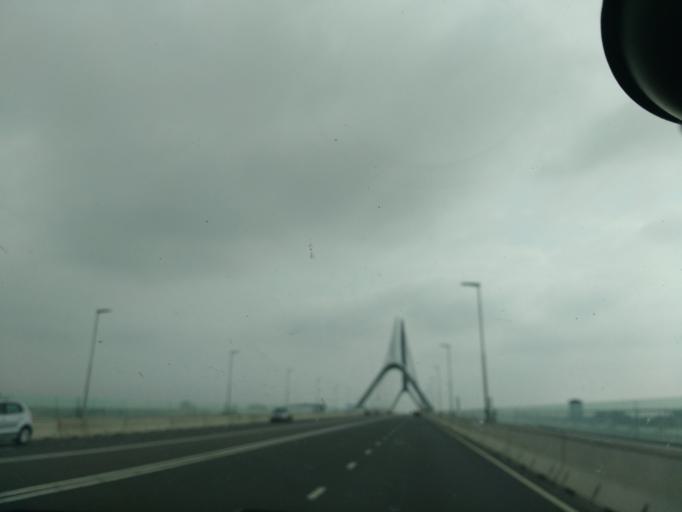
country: NL
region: Gelderland
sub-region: Gemeente Nijmegen
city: Nijmegen
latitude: 51.8611
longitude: 5.8432
